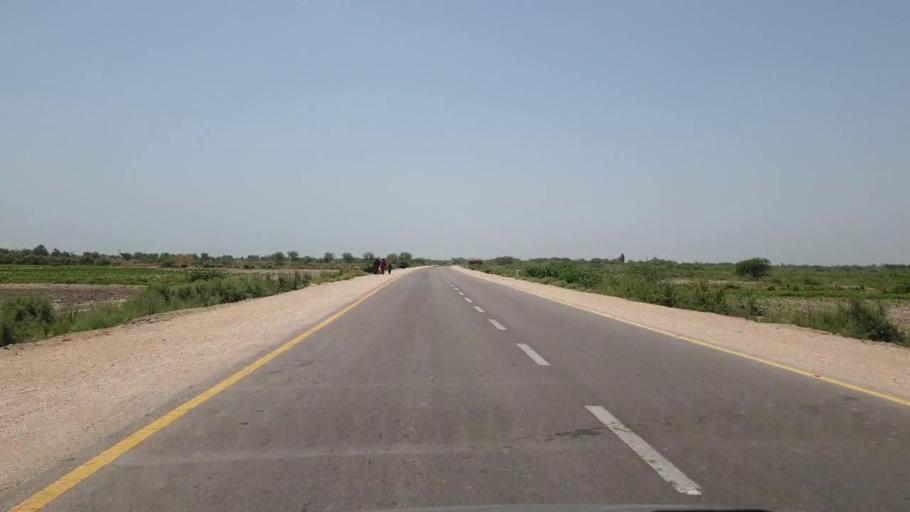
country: PK
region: Sindh
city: Sakrand
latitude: 26.1210
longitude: 68.3839
